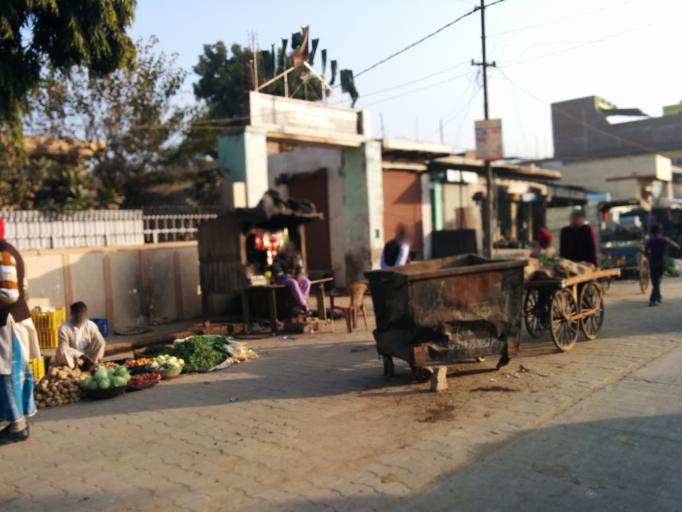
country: IN
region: Uttar Pradesh
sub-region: Mathura
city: Mathura
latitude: 27.5224
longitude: 77.6734
